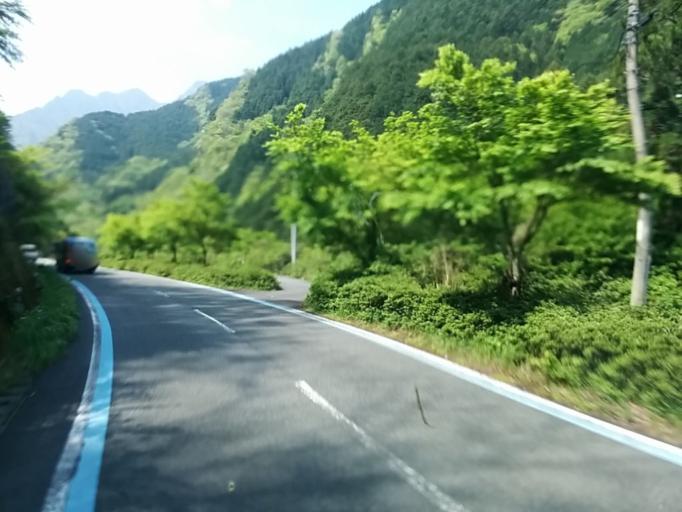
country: JP
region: Ehime
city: Niihama
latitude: 33.8791
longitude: 133.2956
